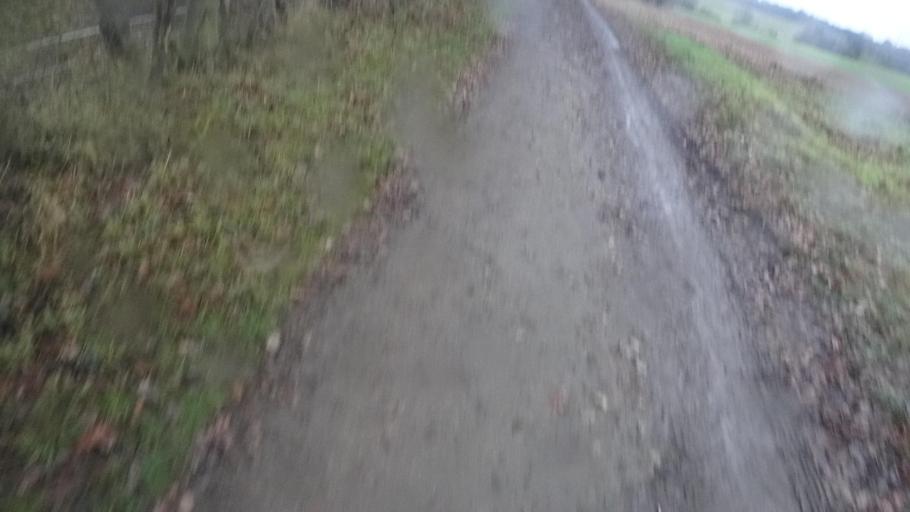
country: DE
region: Rheinland-Pfalz
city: Wiebelsheim
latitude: 50.0732
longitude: 7.6189
